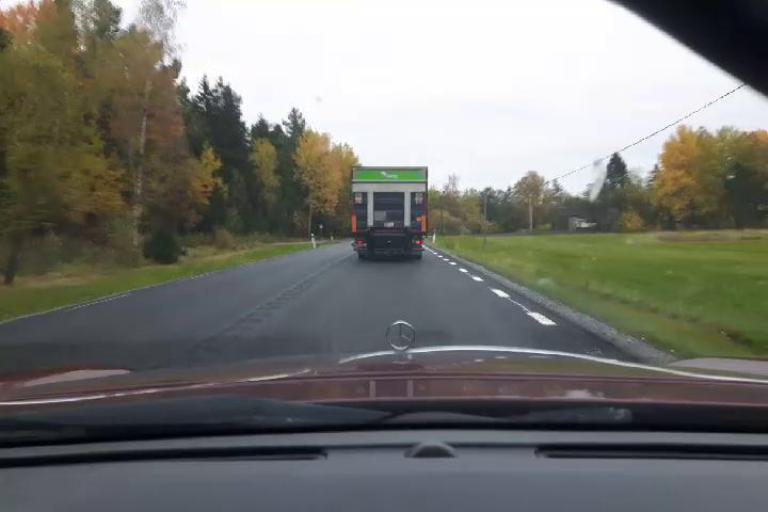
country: SE
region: Soedermanland
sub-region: Strangnas Kommun
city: Strangnas
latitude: 59.4284
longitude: 17.0257
